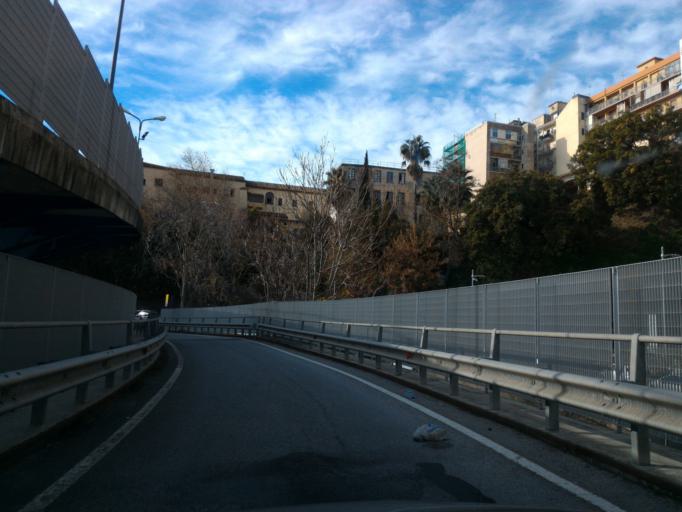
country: IT
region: Calabria
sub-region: Provincia di Catanzaro
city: Siano
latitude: 38.9131
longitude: 16.5896
